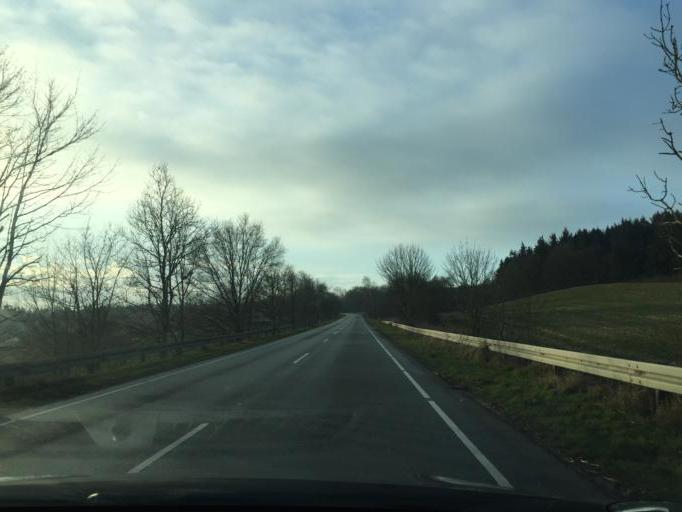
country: DK
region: South Denmark
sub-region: Faaborg-Midtfyn Kommune
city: Faaborg
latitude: 55.1590
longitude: 10.2718
